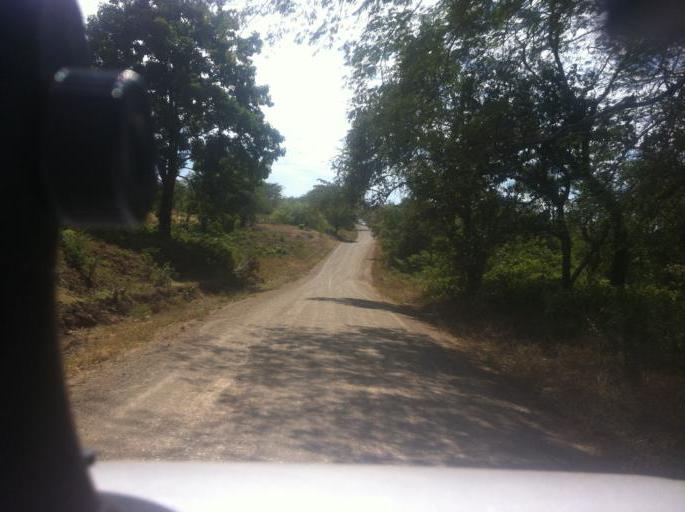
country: NI
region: Rivas
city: Tola
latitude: 11.5519
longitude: -86.0365
